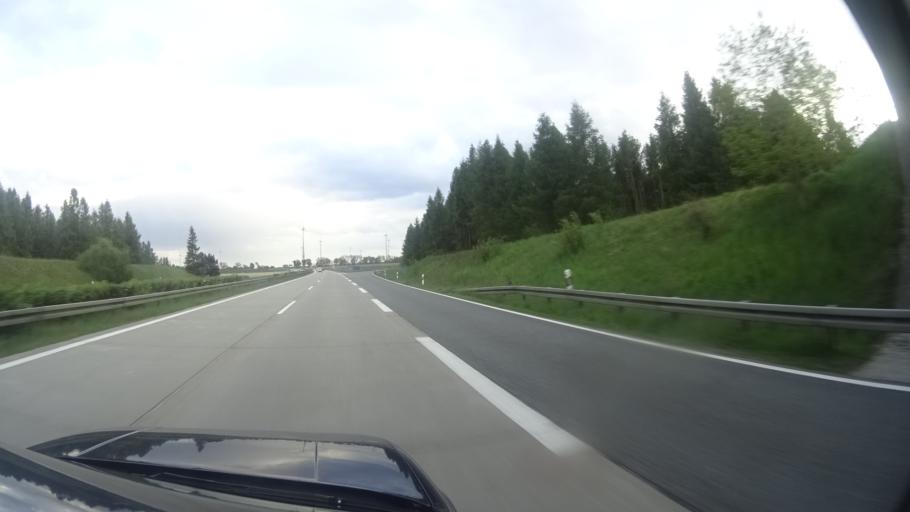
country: DE
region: Brandenburg
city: Wittstock
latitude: 53.1572
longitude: 12.4478
